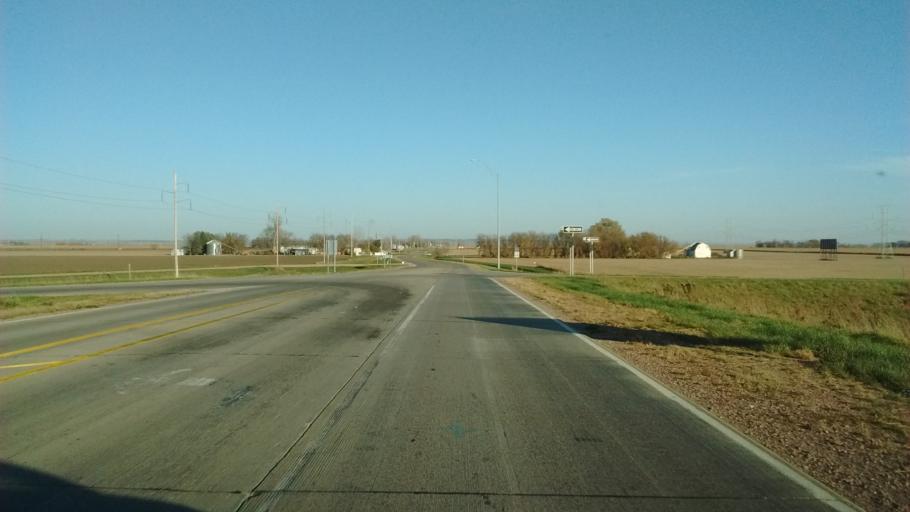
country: US
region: Iowa
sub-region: Woodbury County
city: Sergeant Bluff
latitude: 42.3299
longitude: -96.3170
